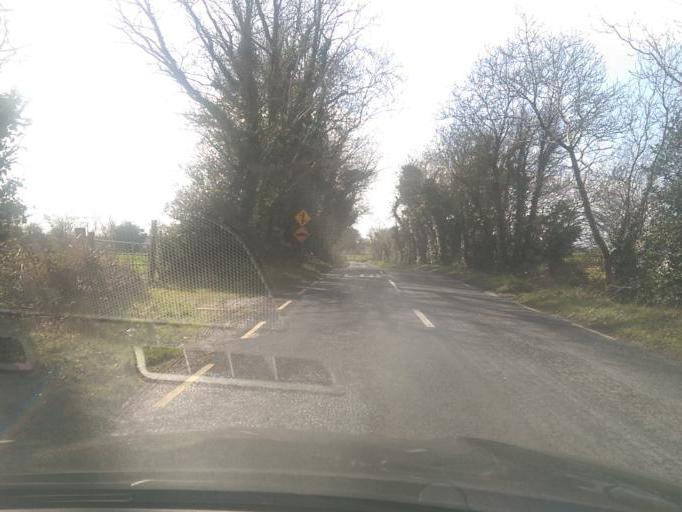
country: IE
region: Connaught
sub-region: County Galway
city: Athenry
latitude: 53.4038
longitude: -8.6419
